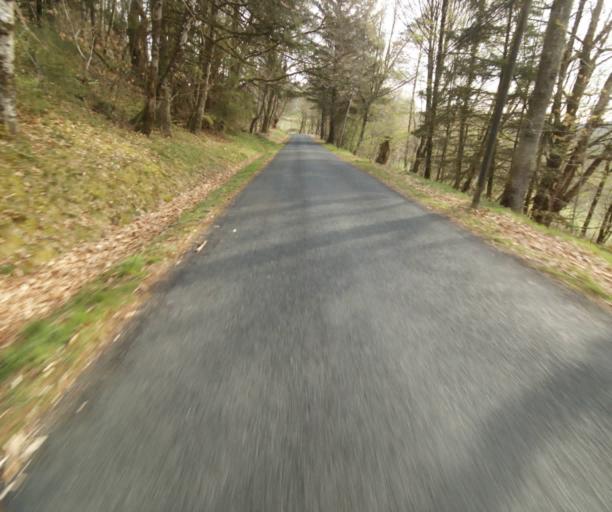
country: FR
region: Limousin
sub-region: Departement de la Correze
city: Correze
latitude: 45.3632
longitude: 1.8603
